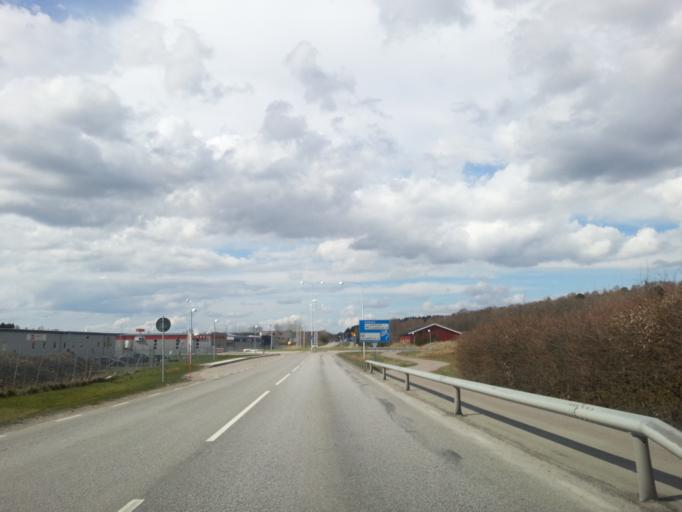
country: SE
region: Vaestra Goetaland
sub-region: Kungalvs Kommun
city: Kungalv
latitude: 57.8902
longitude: 11.9453
